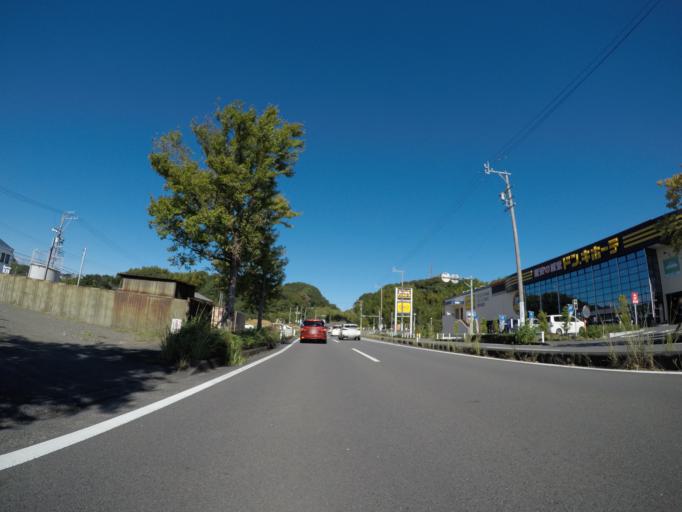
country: JP
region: Shizuoka
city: Fujieda
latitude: 34.8561
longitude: 138.2422
